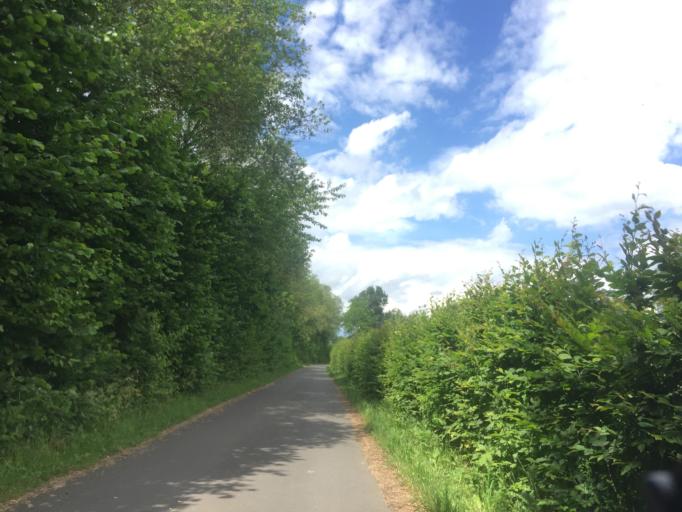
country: DE
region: Rheinland-Pfalz
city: Girod
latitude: 50.4495
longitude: 7.9267
